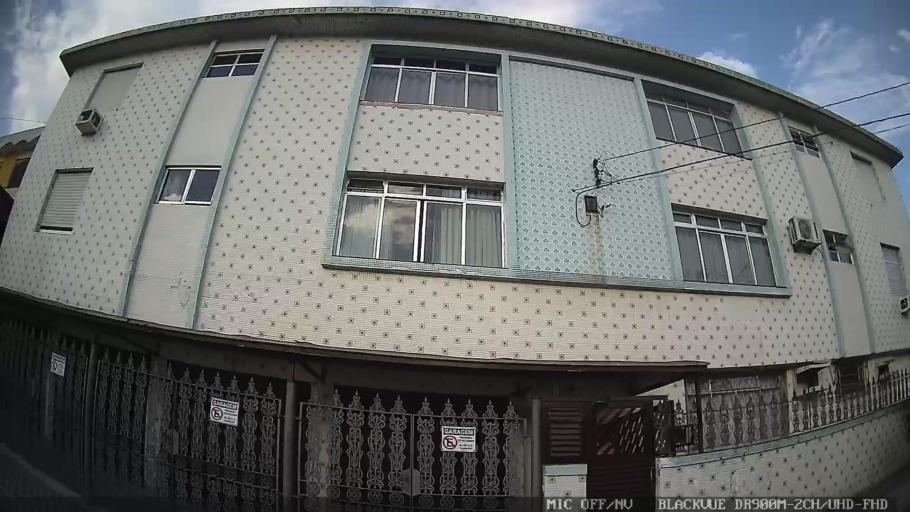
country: BR
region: Sao Paulo
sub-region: Cubatao
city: Cubatao
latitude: -23.8926
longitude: -46.4212
